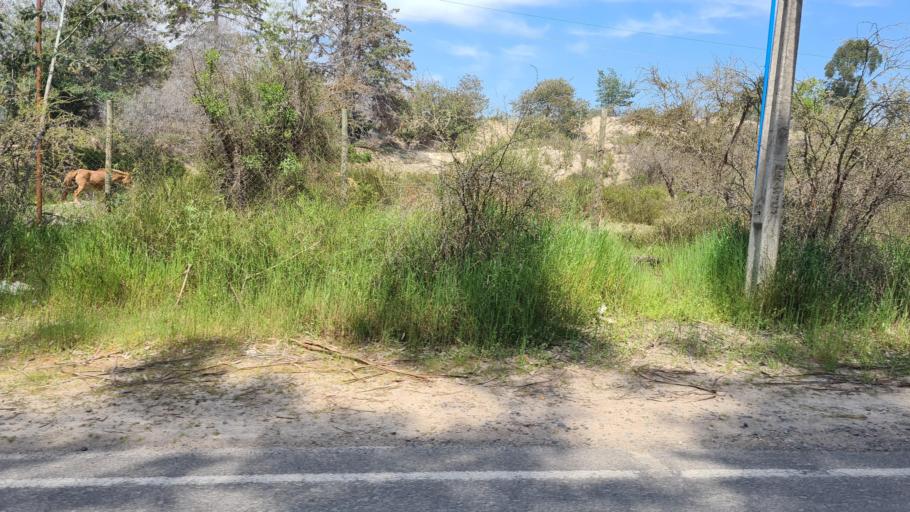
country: CL
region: O'Higgins
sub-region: Provincia de Cachapoal
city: San Vicente
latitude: -34.1506
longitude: -71.4580
